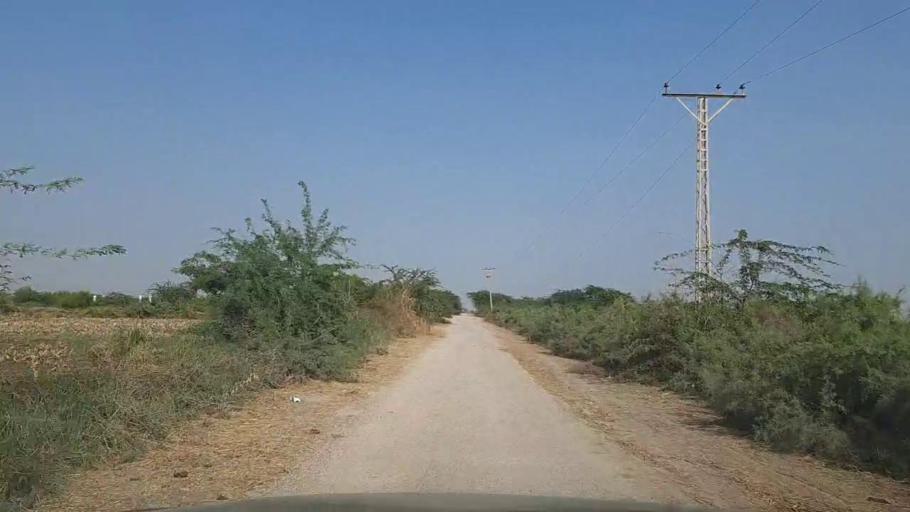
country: PK
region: Sindh
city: Thatta
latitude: 24.6018
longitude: 67.9528
